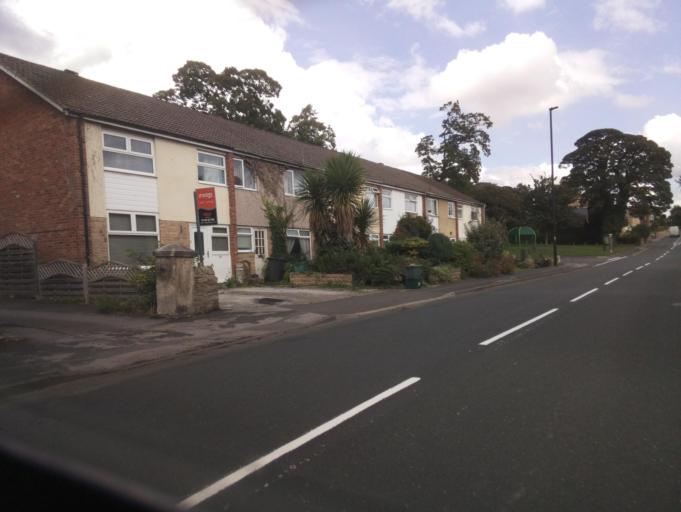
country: GB
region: England
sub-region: North Yorkshire
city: Catterick Garrison
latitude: 54.4050
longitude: -1.7518
